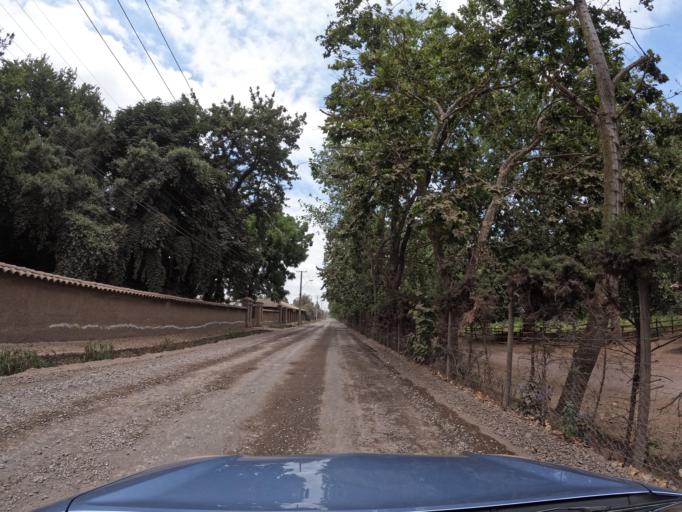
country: CL
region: O'Higgins
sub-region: Provincia de Colchagua
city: Chimbarongo
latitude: -34.7373
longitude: -70.9761
